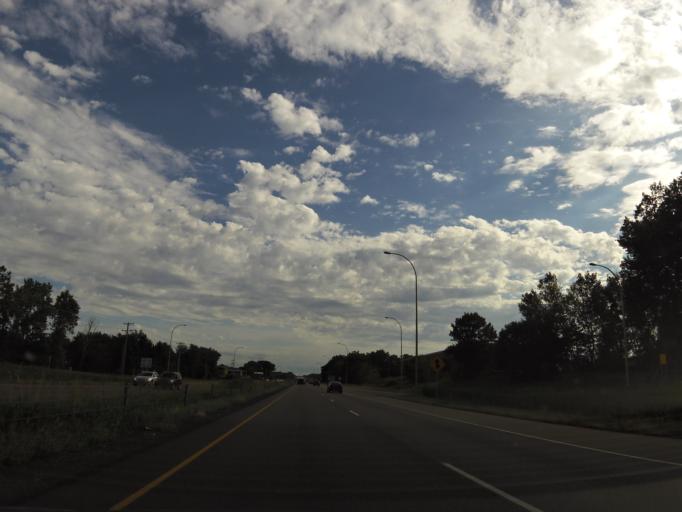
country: US
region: Minnesota
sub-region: Hennepin County
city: New Hope
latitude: 45.0430
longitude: -93.4010
